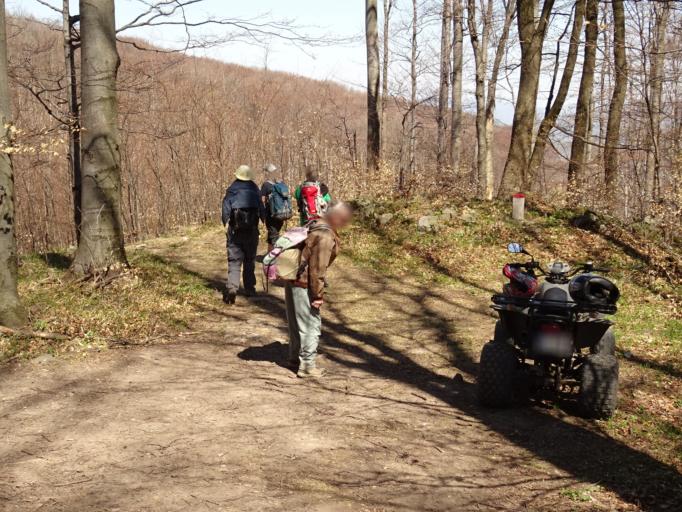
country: HU
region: Borsod-Abauj-Zemplen
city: Gonc
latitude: 48.5738
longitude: 21.4606
